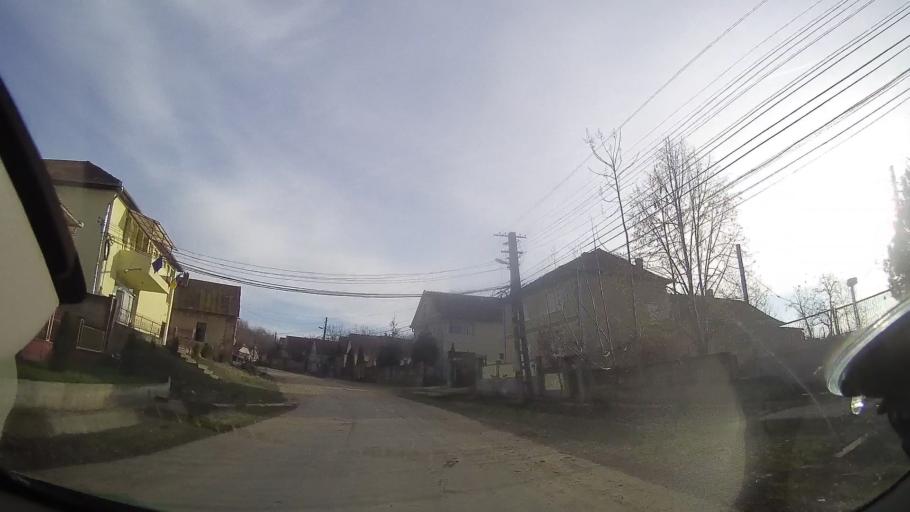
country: RO
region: Bihor
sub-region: Comuna Sarbi
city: Burzuc
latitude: 47.1545
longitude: 22.1700
